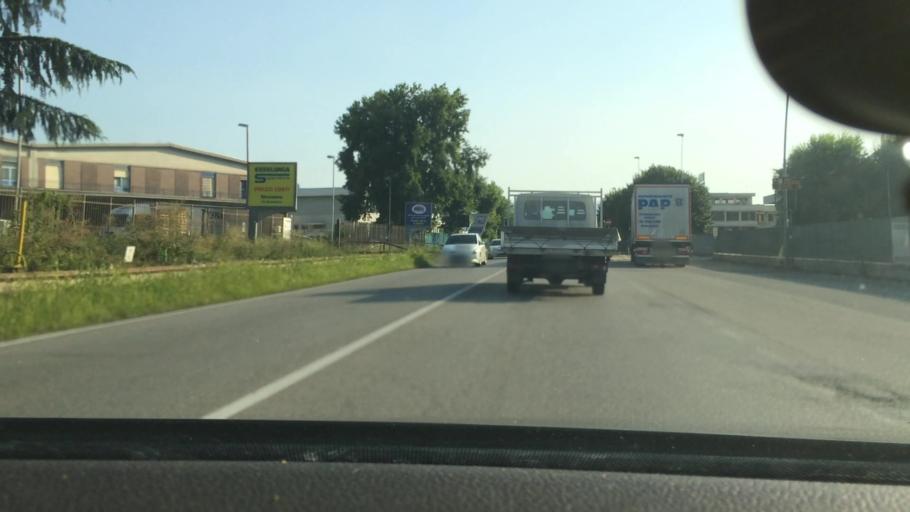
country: IT
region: Lombardy
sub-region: Provincia di Bergamo
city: Lallio
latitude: 45.6602
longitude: 9.6294
